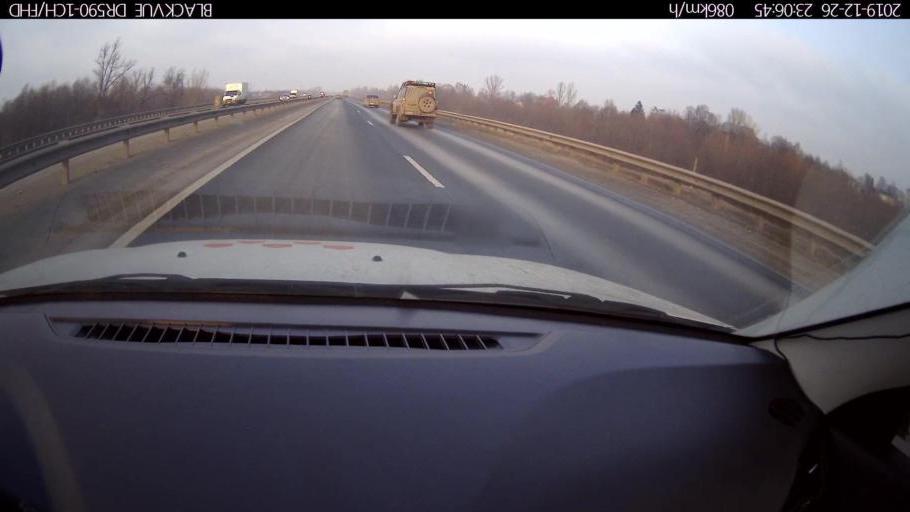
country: RU
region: Nizjnij Novgorod
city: Gorbatovka
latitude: 56.2087
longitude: 43.7519
